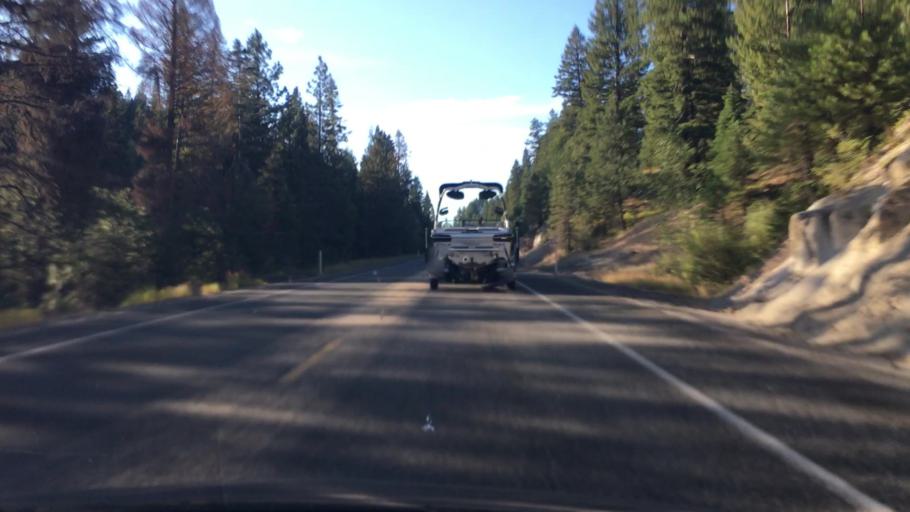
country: US
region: Idaho
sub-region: Valley County
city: Cascade
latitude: 44.5729
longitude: -116.0319
